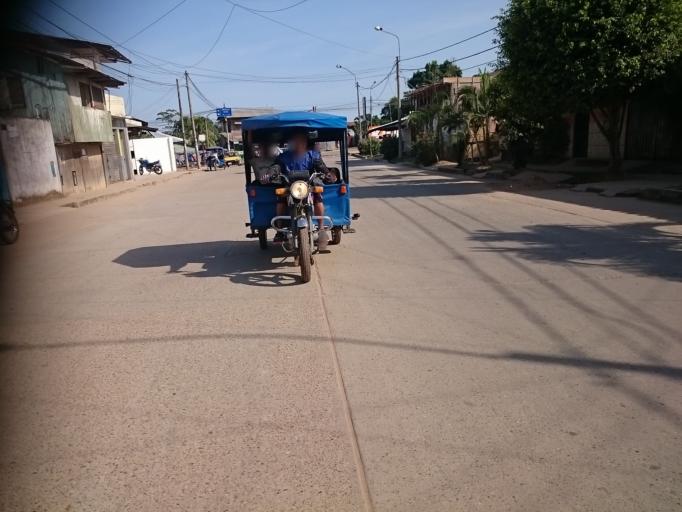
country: PE
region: Ucayali
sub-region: Provincia de Coronel Portillo
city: Puerto Callao
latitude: -8.3537
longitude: -74.5775
